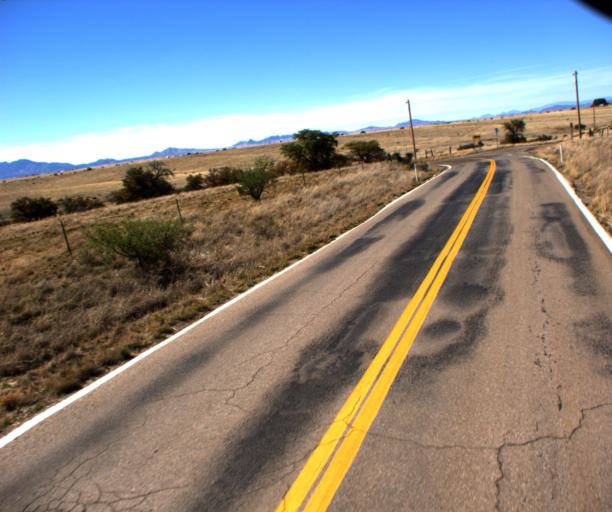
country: US
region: Arizona
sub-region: Cochise County
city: Huachuca City
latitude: 31.5999
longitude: -110.5583
